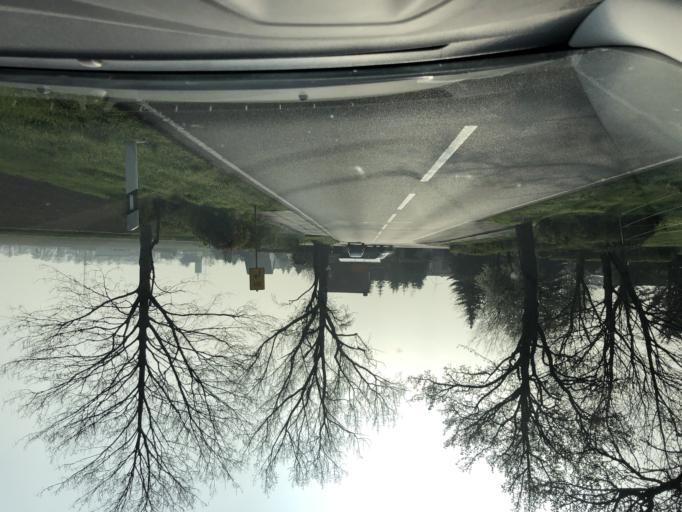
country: DE
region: Saxony-Anhalt
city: Zorbig
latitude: 51.5878
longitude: 12.1376
